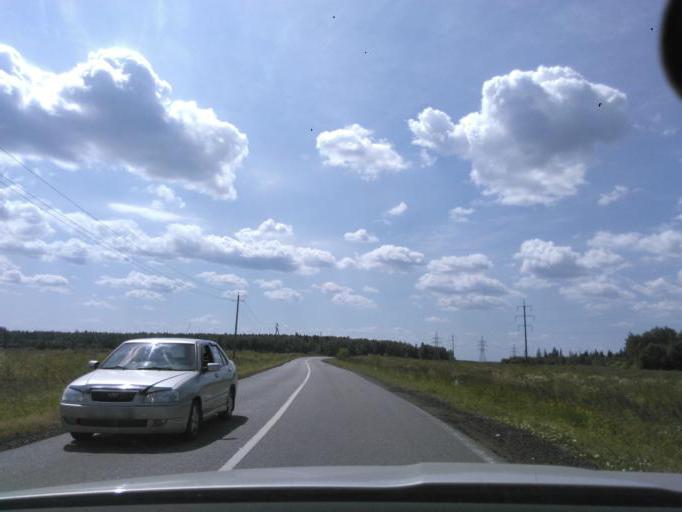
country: RU
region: Moskovskaya
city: Solnechnogorsk
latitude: 56.1468
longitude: 36.9788
